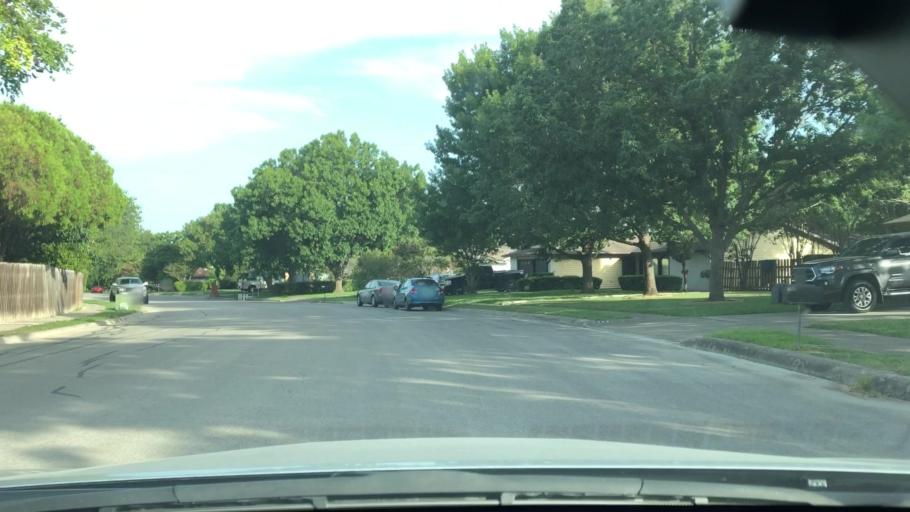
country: US
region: Texas
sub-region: Bexar County
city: Converse
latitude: 29.5346
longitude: -98.3237
